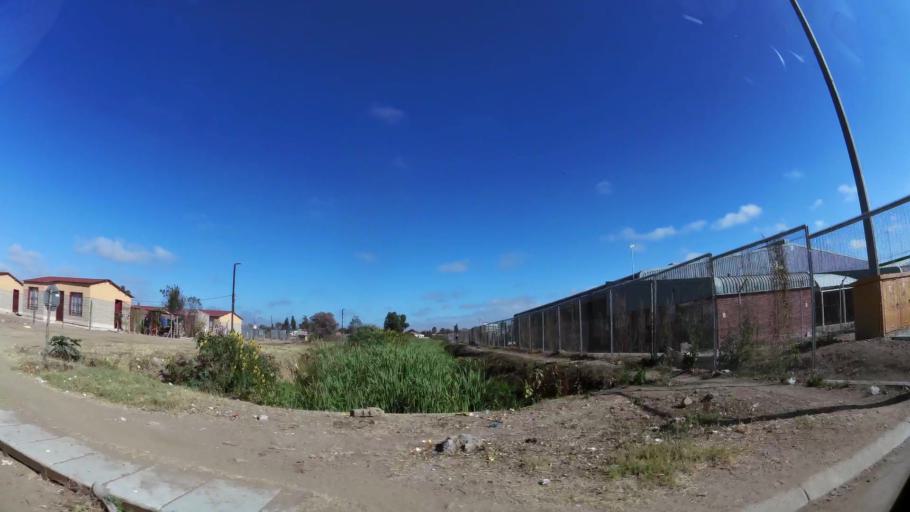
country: ZA
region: Limpopo
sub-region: Capricorn District Municipality
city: Polokwane
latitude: -23.8461
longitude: 29.4002
